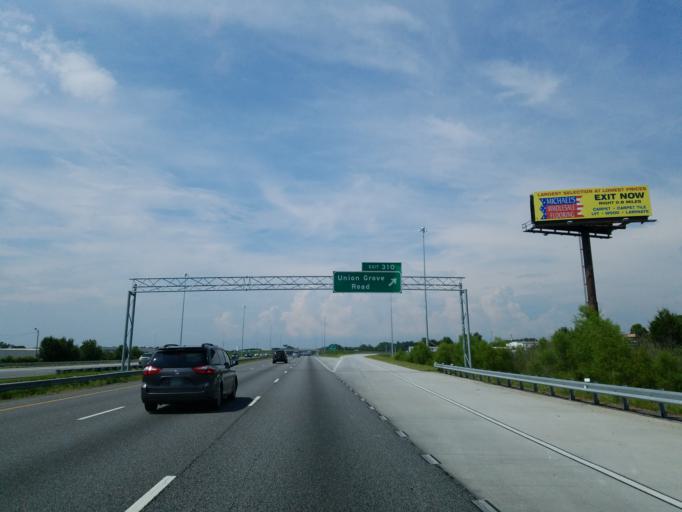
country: US
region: Georgia
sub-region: Bartow County
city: Adairsville
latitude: 34.4349
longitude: -84.9201
